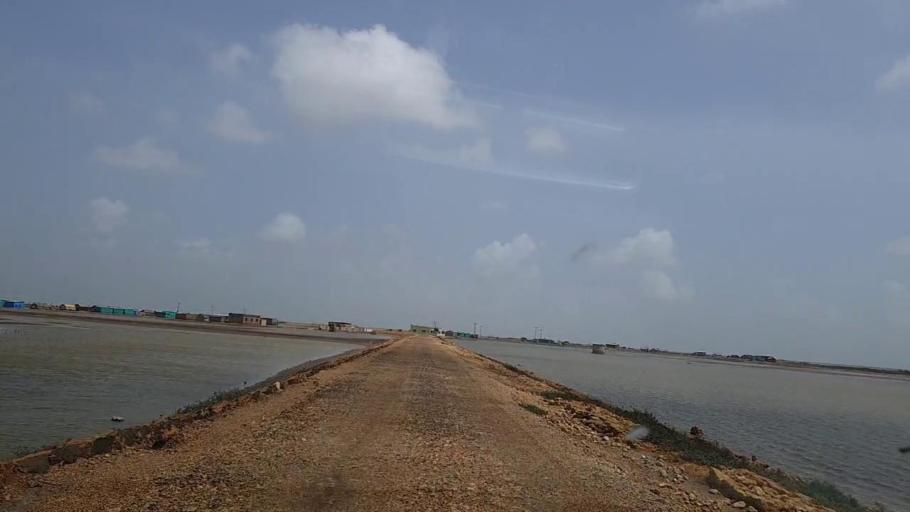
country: PK
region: Sindh
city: Keti Bandar
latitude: 24.1309
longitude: 67.4658
